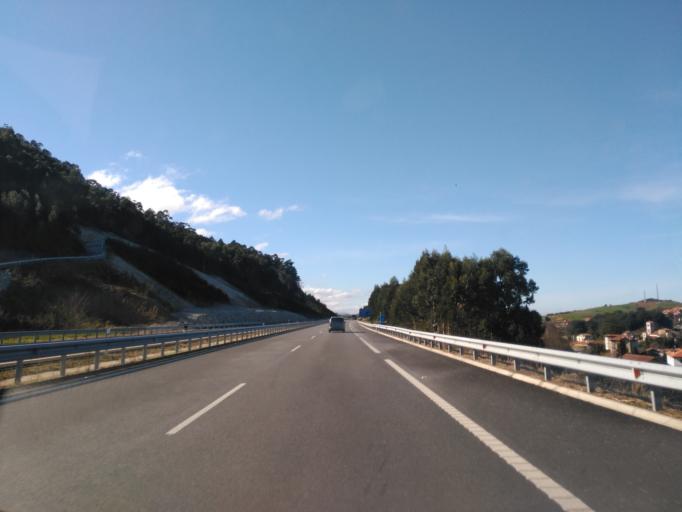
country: ES
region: Asturias
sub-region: Province of Asturias
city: Llanes
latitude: 43.3920
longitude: -4.6284
